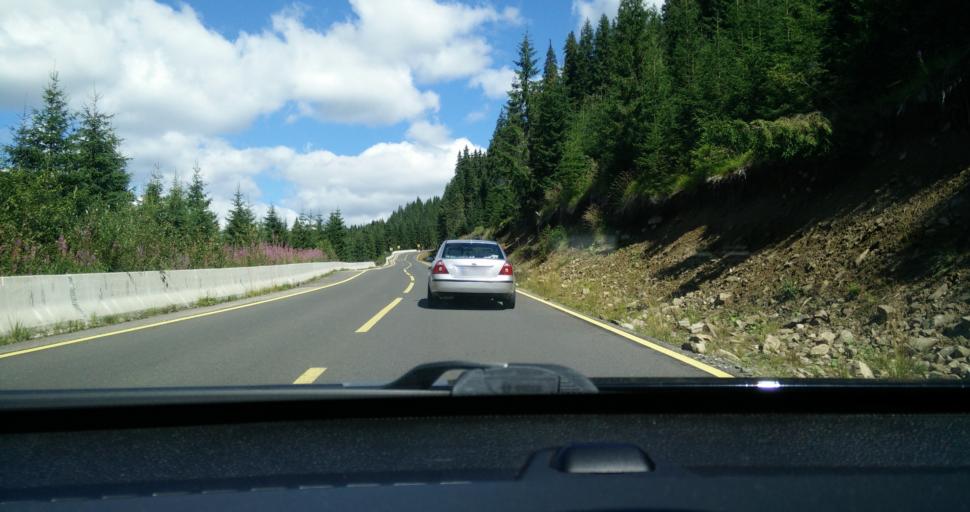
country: RO
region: Hunedoara
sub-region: Oras Petrila
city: Petrila
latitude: 45.4467
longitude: 23.6217
